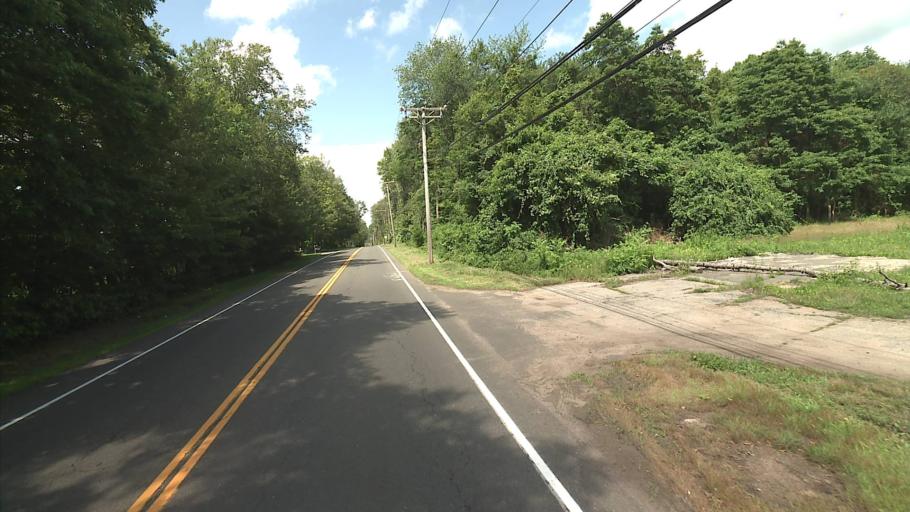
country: US
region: Connecticut
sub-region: Middlesex County
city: Higganum
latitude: 41.4213
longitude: -72.5629
